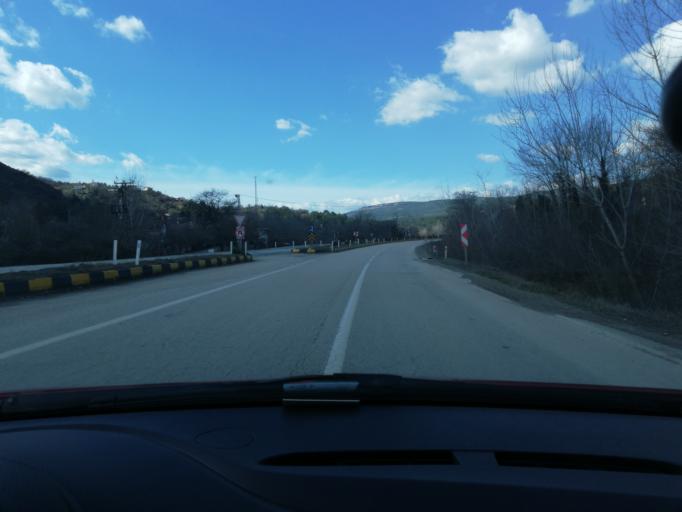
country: TR
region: Karabuk
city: Ovacik
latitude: 41.1977
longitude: 32.9142
